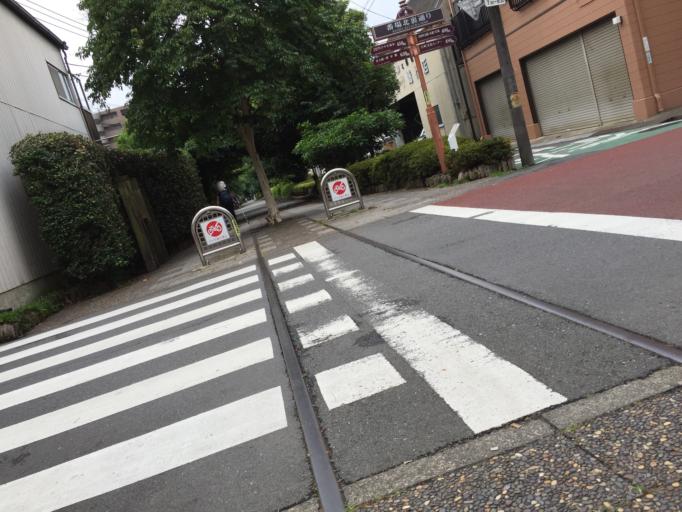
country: JP
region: Tokyo
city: Kokubunji
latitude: 35.6711
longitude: 139.4738
